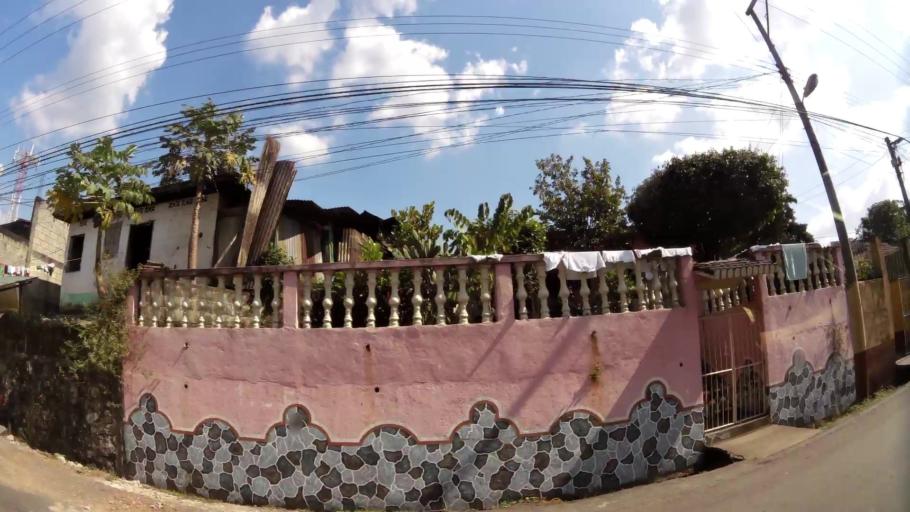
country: GT
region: Suchitepeque
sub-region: Municipio de Cuyotenango
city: Cuyotenango
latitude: 14.5369
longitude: -91.5729
